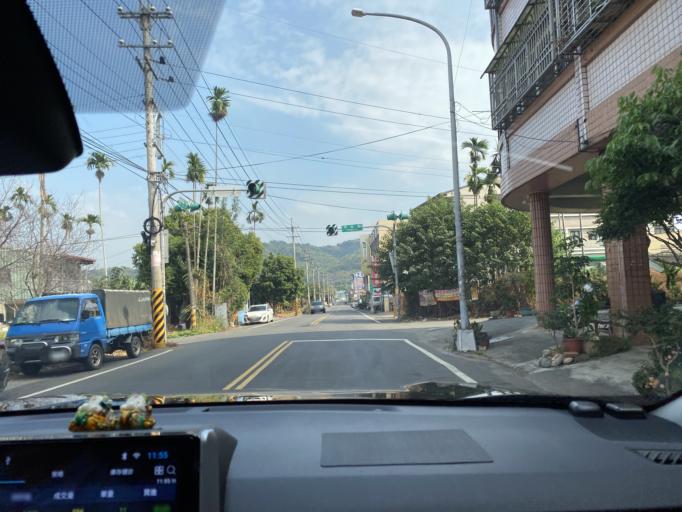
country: TW
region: Taiwan
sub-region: Nantou
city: Nantou
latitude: 23.8418
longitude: 120.6919
